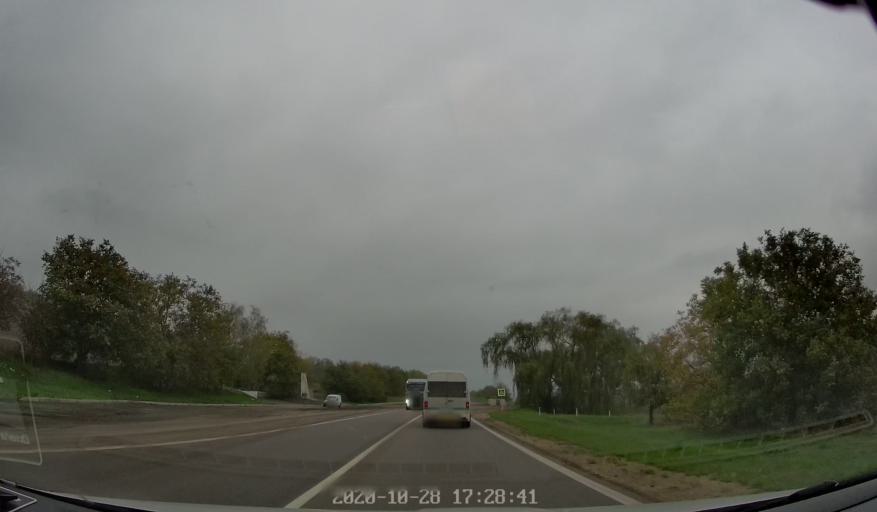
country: MD
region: Cimislia
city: Cimislia
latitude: 46.6632
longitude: 28.6983
